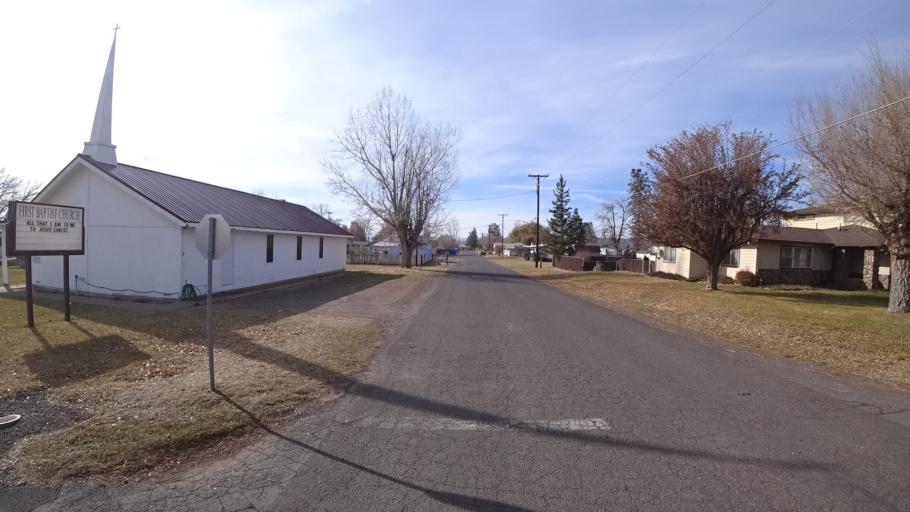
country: US
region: Oregon
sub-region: Klamath County
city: Klamath Falls
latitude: 41.9686
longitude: -121.9184
